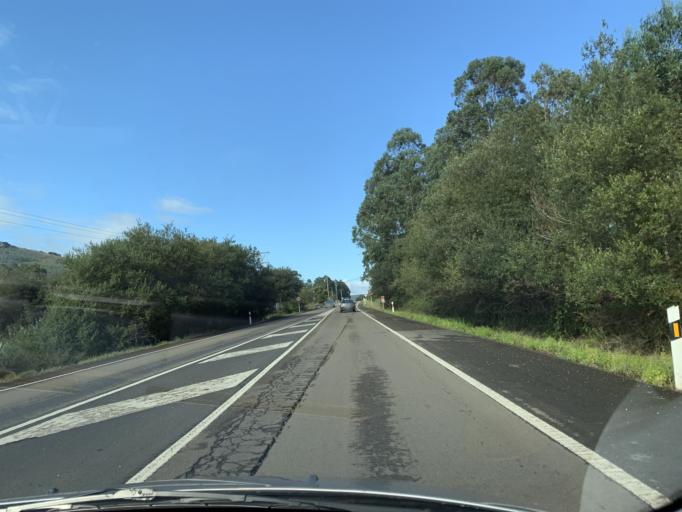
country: ES
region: Galicia
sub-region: Provincia de Lugo
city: Barreiros
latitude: 43.5458
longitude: -7.1580
